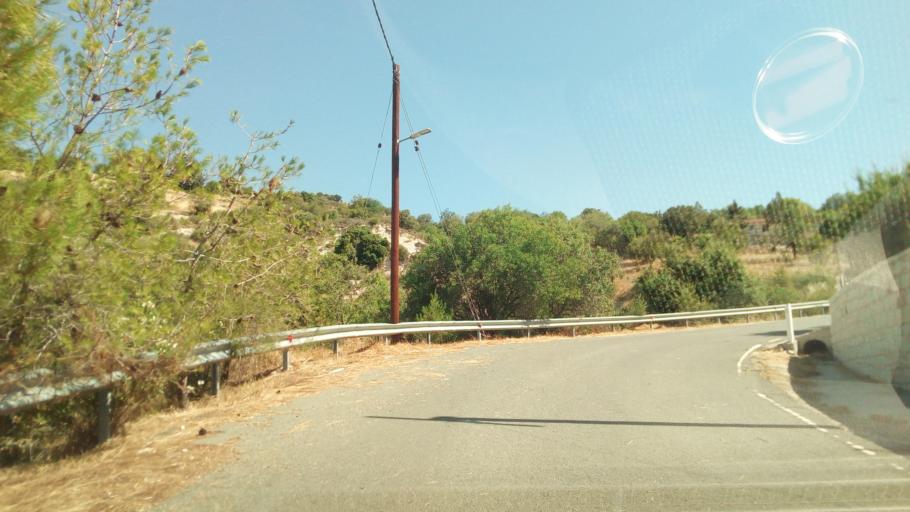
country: CY
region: Limassol
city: Pachna
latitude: 34.8013
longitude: 32.6781
